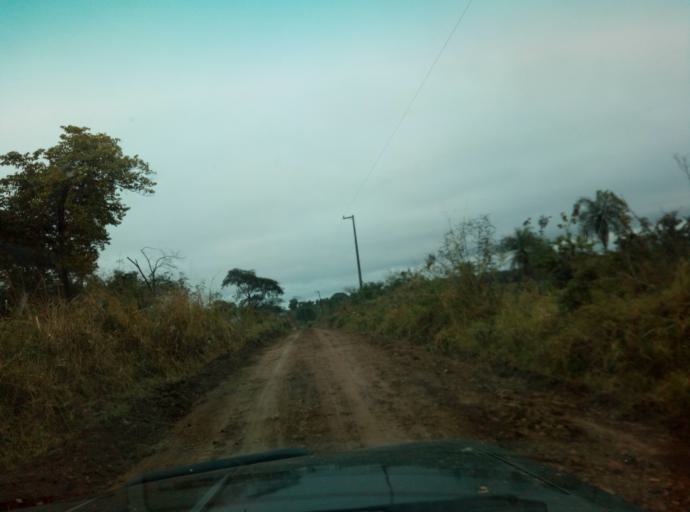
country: PY
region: Caaguazu
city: Carayao
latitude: -25.1903
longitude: -56.3698
